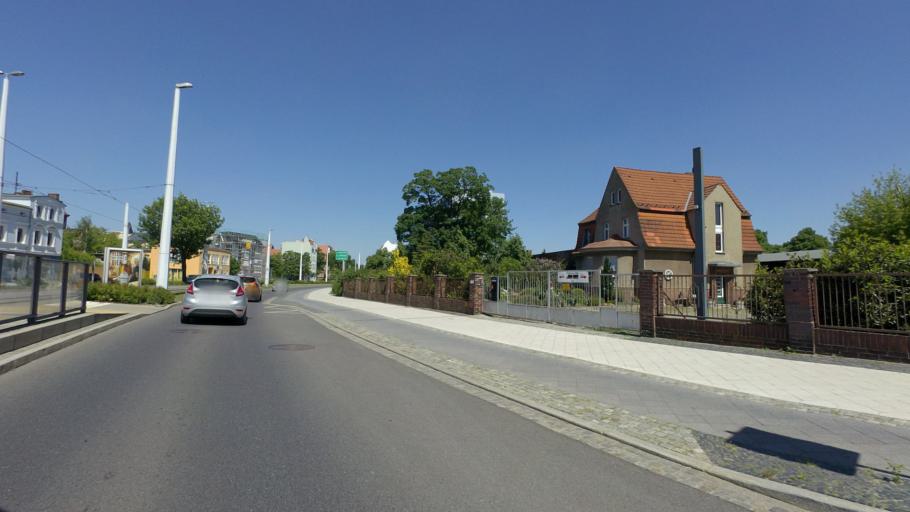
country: DE
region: Brandenburg
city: Cottbus
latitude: 51.7451
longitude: 14.3316
